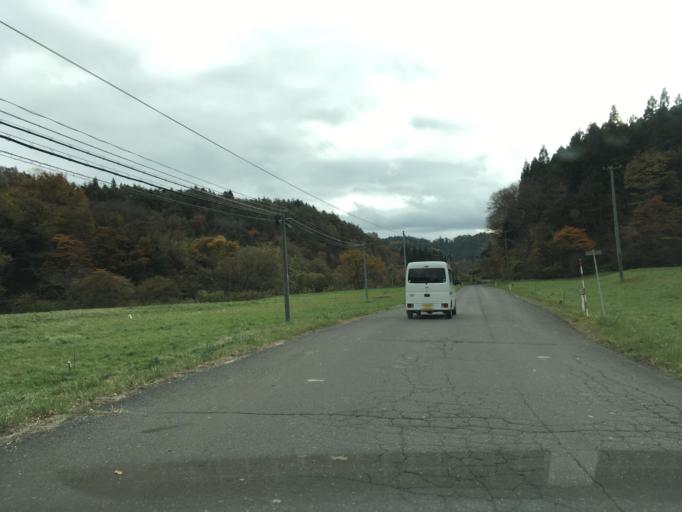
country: JP
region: Iwate
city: Mizusawa
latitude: 39.0880
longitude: 141.3493
